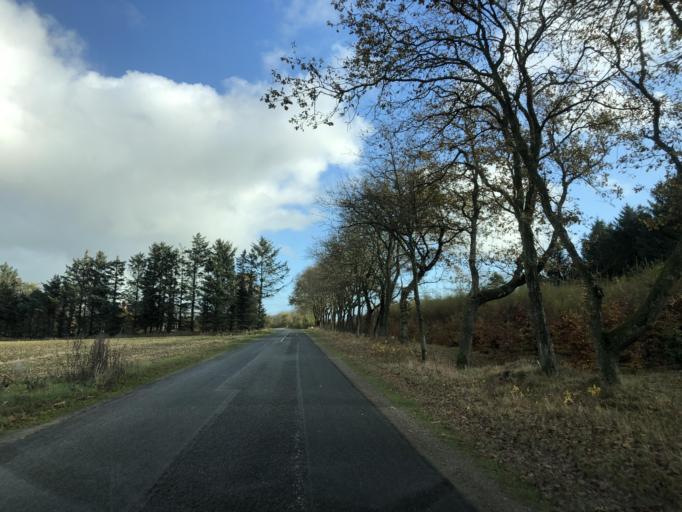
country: DK
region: Central Jutland
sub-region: Ringkobing-Skjern Kommune
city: Ringkobing
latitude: 56.1376
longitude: 8.3416
